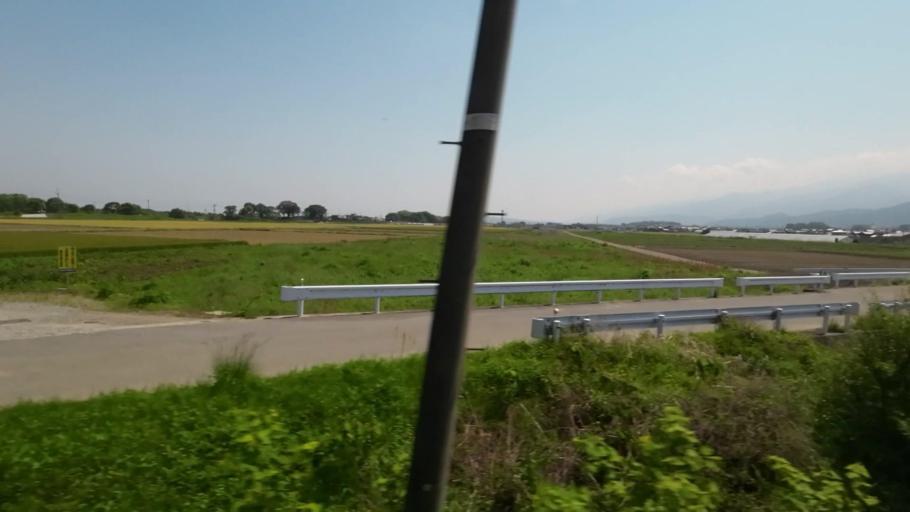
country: JP
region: Ehime
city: Saijo
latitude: 33.9019
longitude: 133.0998
